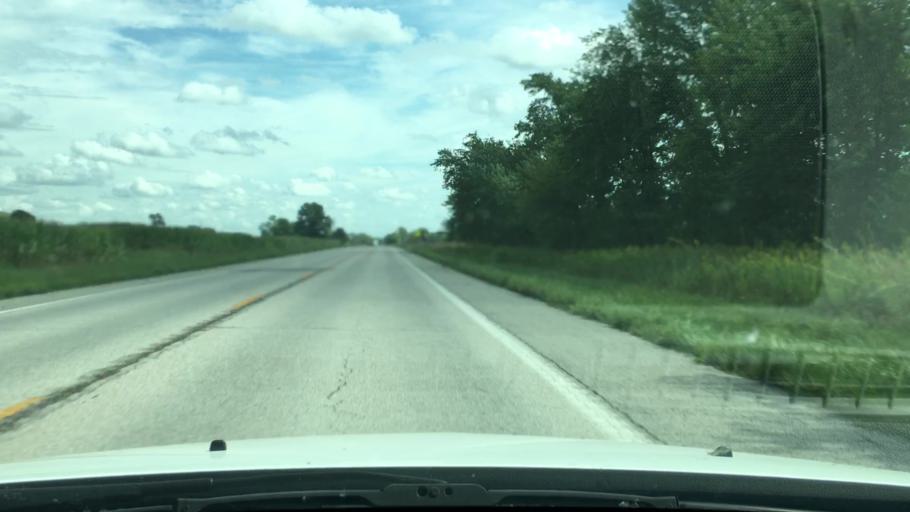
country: US
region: Missouri
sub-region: Audrain County
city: Vandalia
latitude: 39.2960
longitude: -91.5198
